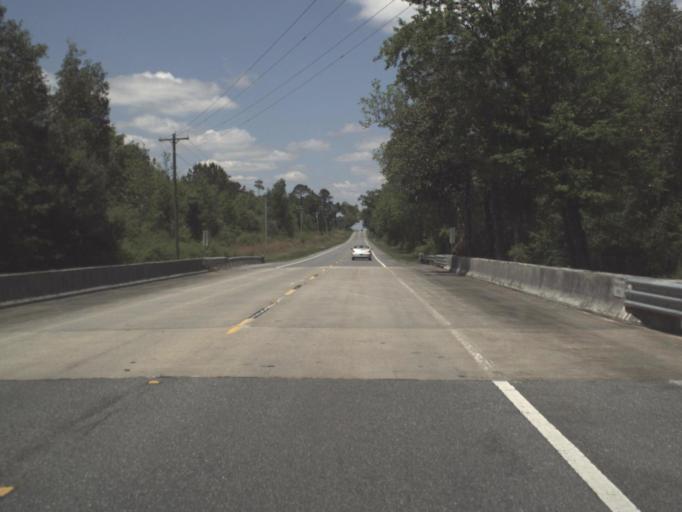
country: US
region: Florida
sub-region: Santa Rosa County
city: Point Baker
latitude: 30.8019
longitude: -87.0422
